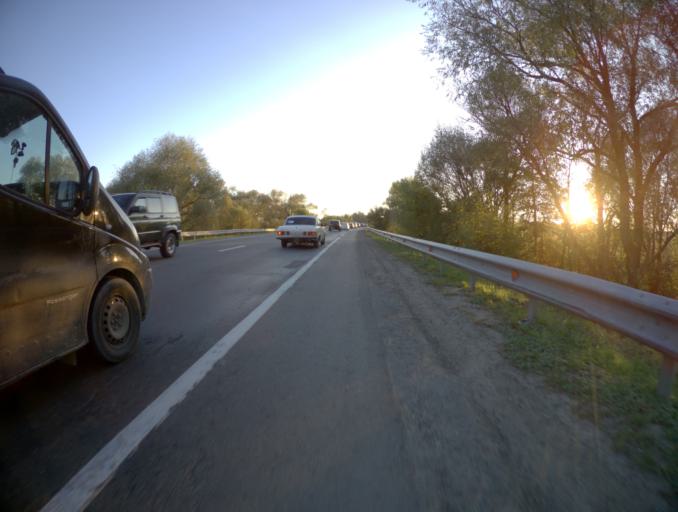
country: RU
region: Vladimir
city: Bogolyubovo
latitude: 56.2056
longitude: 40.5643
